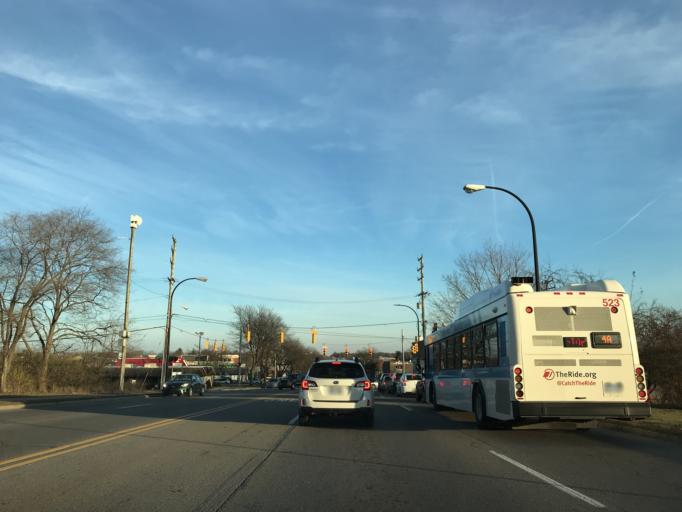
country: US
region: Michigan
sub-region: Washtenaw County
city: Ann Arbor
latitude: 42.2579
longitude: -83.7015
